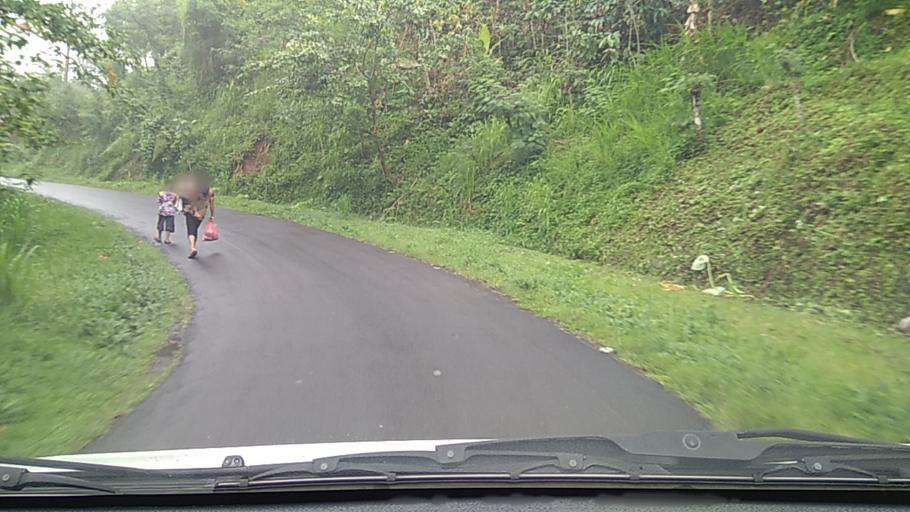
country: ID
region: Bali
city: Banjar Ambengan
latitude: -8.1971
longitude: 115.1817
